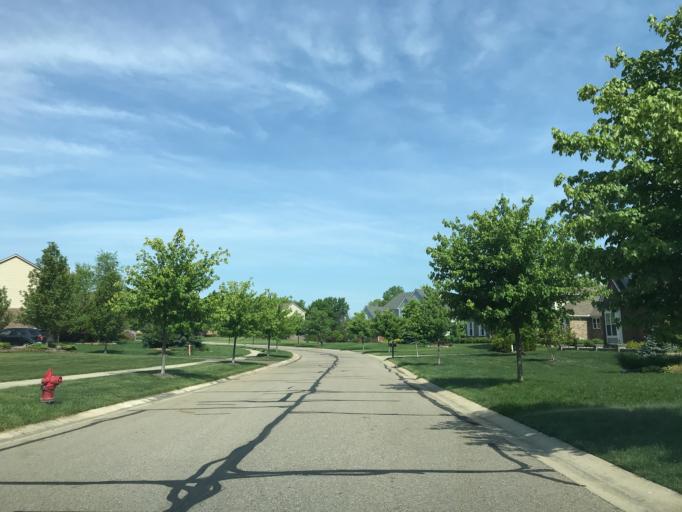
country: US
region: Michigan
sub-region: Oakland County
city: South Lyon
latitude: 42.4814
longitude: -83.6343
